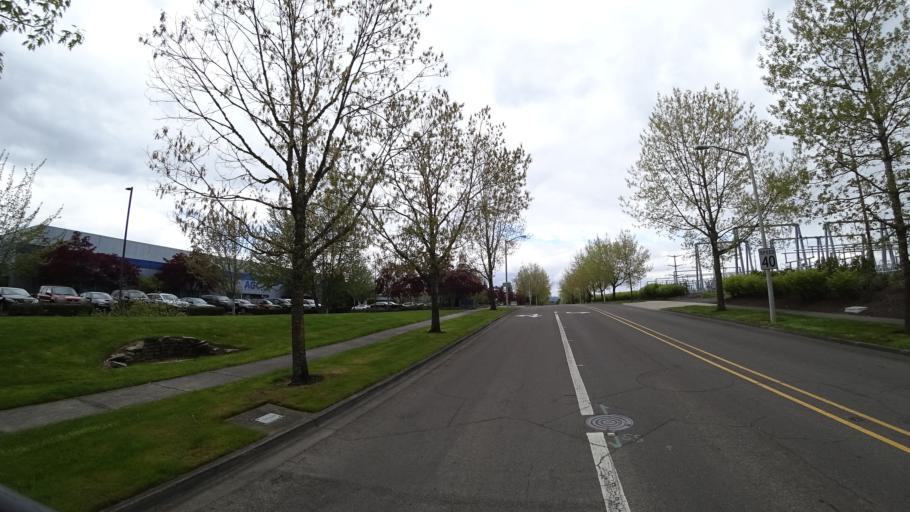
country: US
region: Oregon
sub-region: Washington County
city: Rockcreek
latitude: 45.5512
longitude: -122.9184
